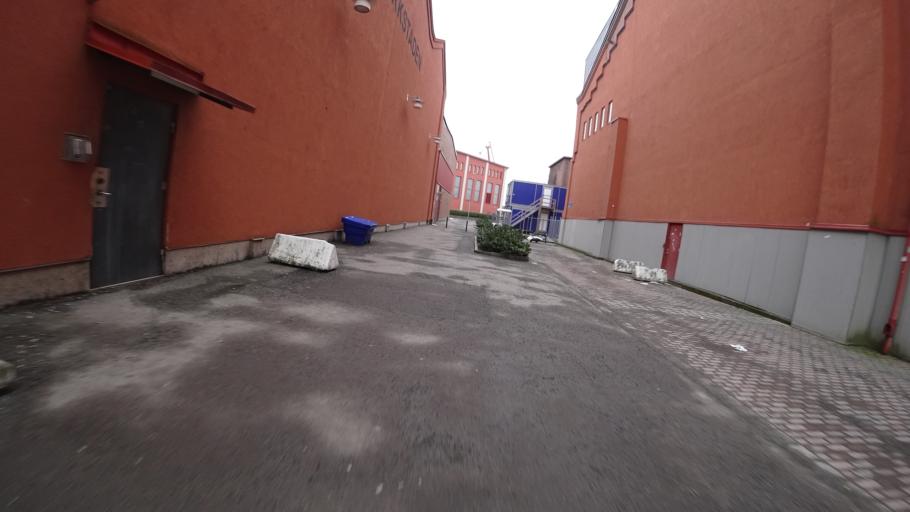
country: SE
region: Vaestra Goetaland
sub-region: Goteborg
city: Goeteborg
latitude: 57.7093
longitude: 11.9462
